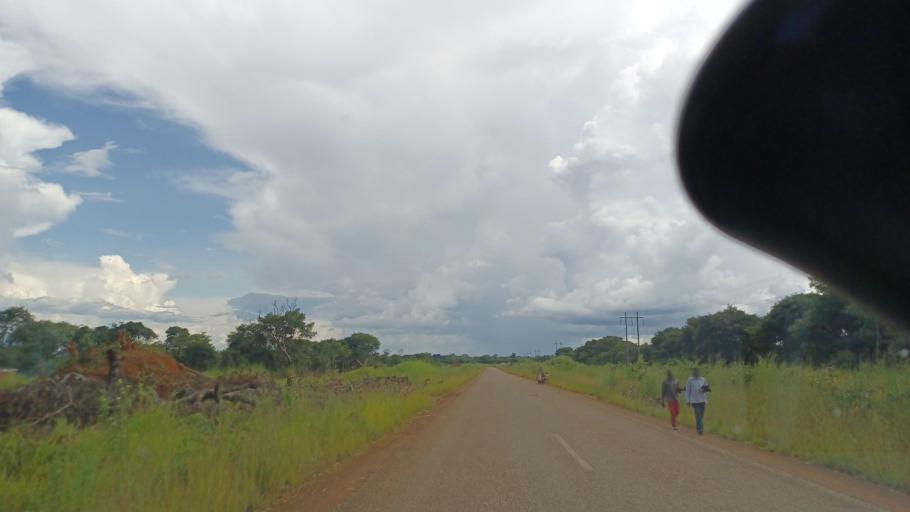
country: ZM
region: North-Western
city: Kasempa
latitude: -13.1172
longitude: 25.8701
